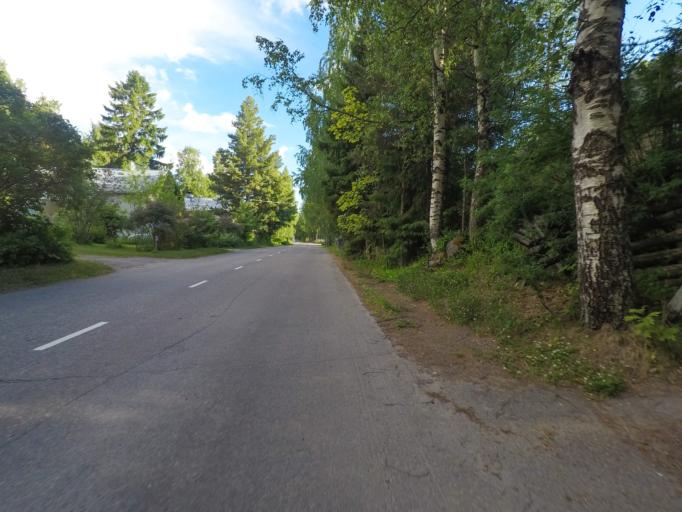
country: FI
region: Southern Savonia
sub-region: Savonlinna
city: Savonlinna
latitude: 61.8780
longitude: 28.8557
